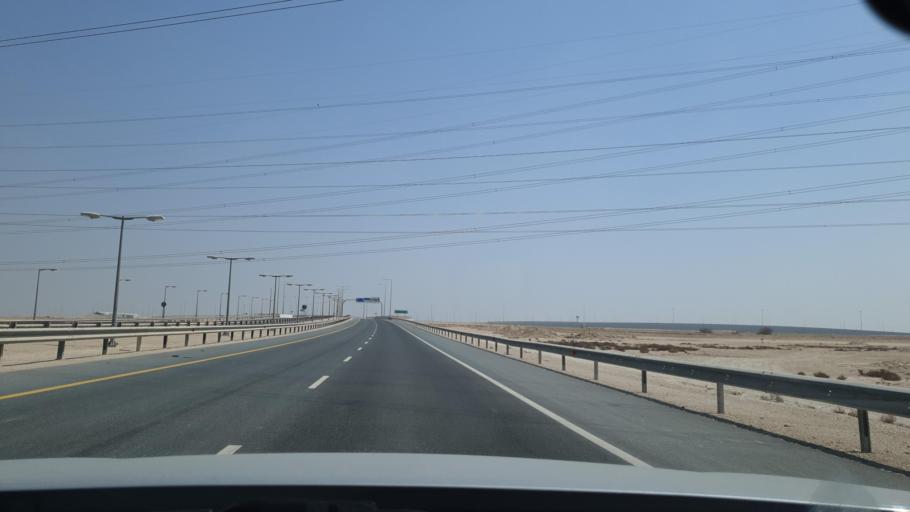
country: QA
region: Baladiyat az Za`ayin
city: Az Za`ayin
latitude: 25.6186
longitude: 51.3559
